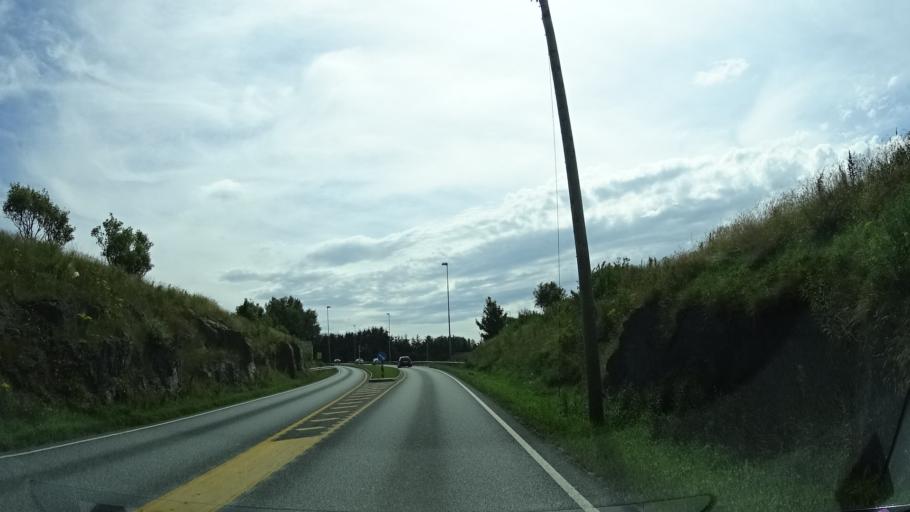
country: NO
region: Rogaland
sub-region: Randaberg
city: Randaberg
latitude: 58.9923
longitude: 5.6531
